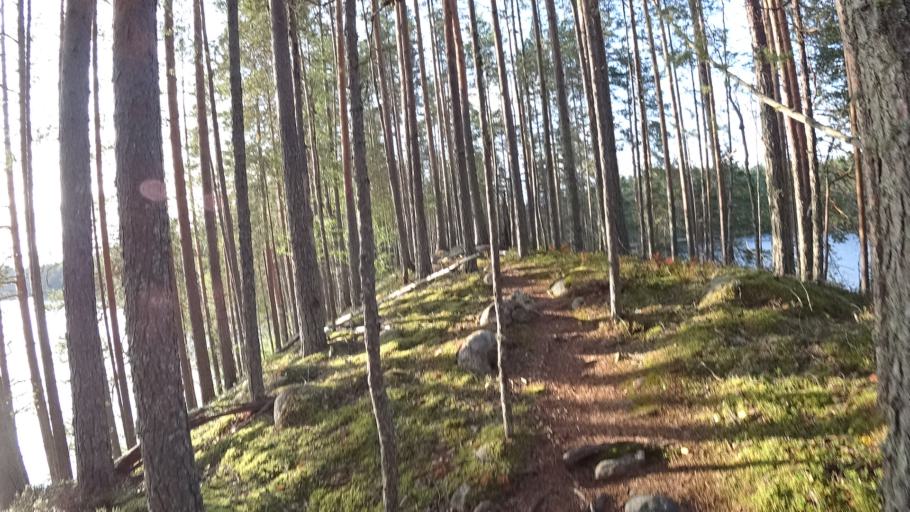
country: FI
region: North Karelia
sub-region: Joensuu
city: Ilomantsi
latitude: 62.5770
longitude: 31.1721
